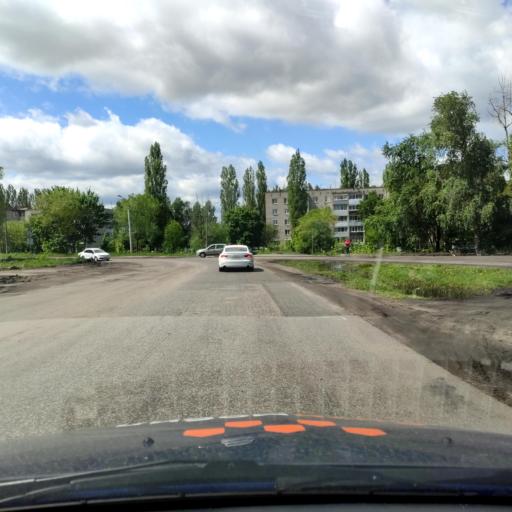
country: RU
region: Voronezj
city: Maslovka
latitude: 51.5880
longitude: 39.3236
